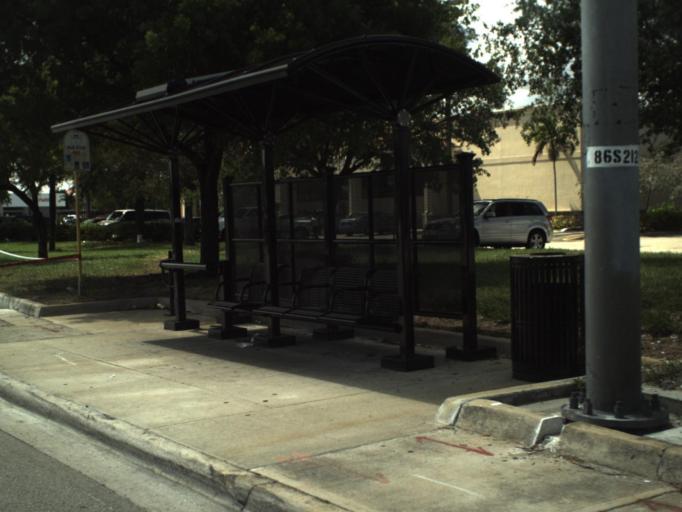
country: US
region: Florida
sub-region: Broward County
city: West Park
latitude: 25.9952
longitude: -80.2059
